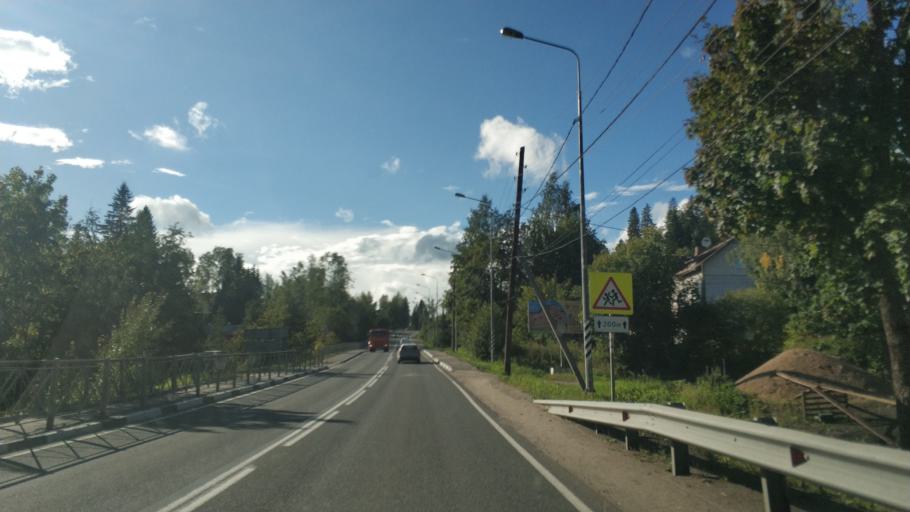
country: RU
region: Republic of Karelia
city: Lakhdenpokh'ya
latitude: 61.5215
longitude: 30.1908
